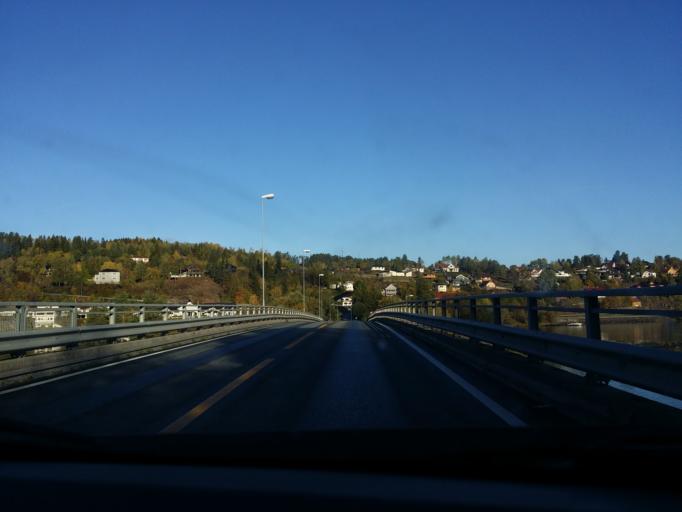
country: NO
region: Buskerud
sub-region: Hole
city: Vik
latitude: 60.0635
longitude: 10.3009
